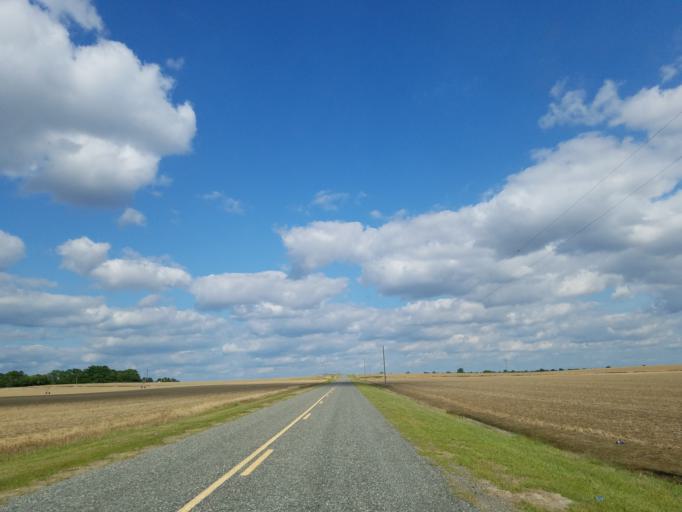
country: US
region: Georgia
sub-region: Dooly County
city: Unadilla
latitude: 32.2366
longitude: -83.7644
